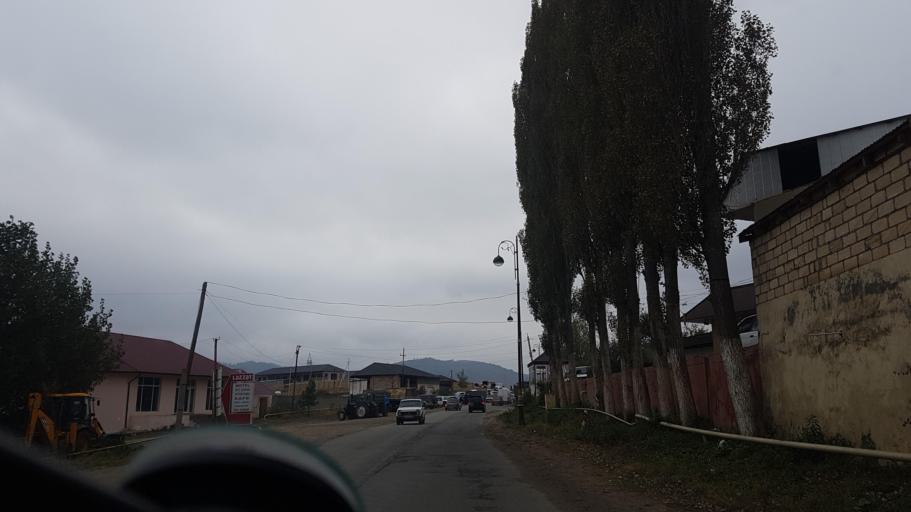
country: AZ
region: Gadabay Rayon
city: Ariqdam
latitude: 40.5934
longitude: 45.8112
